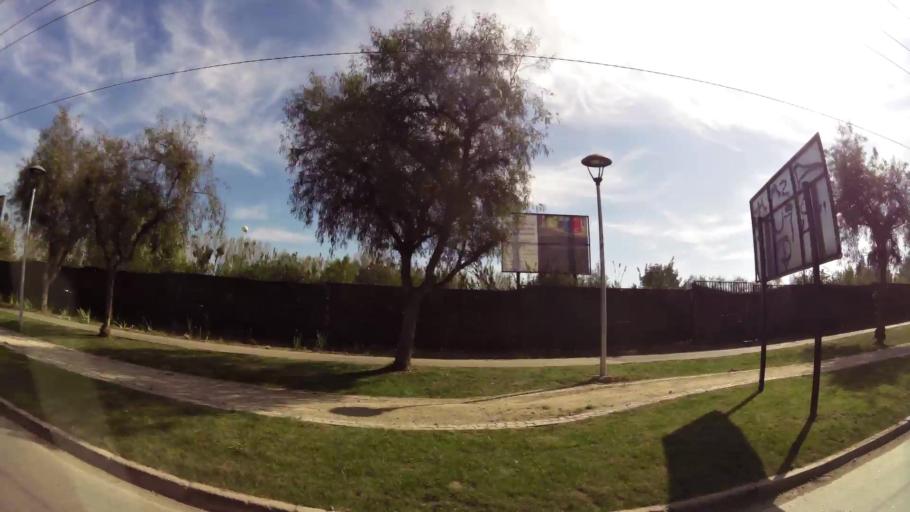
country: CL
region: Santiago Metropolitan
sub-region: Provincia de Santiago
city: Villa Presidente Frei, Nunoa, Santiago, Chile
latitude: -33.4339
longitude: -70.5423
